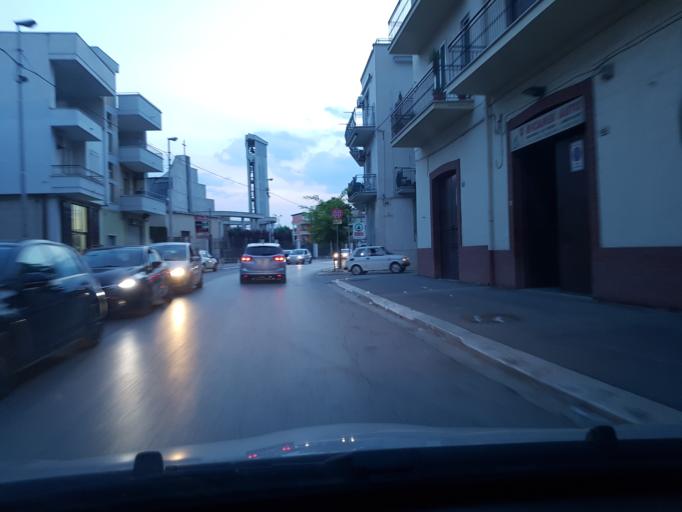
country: IT
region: Apulia
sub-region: Provincia di Foggia
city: Cerignola
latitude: 41.2596
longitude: 15.8947
